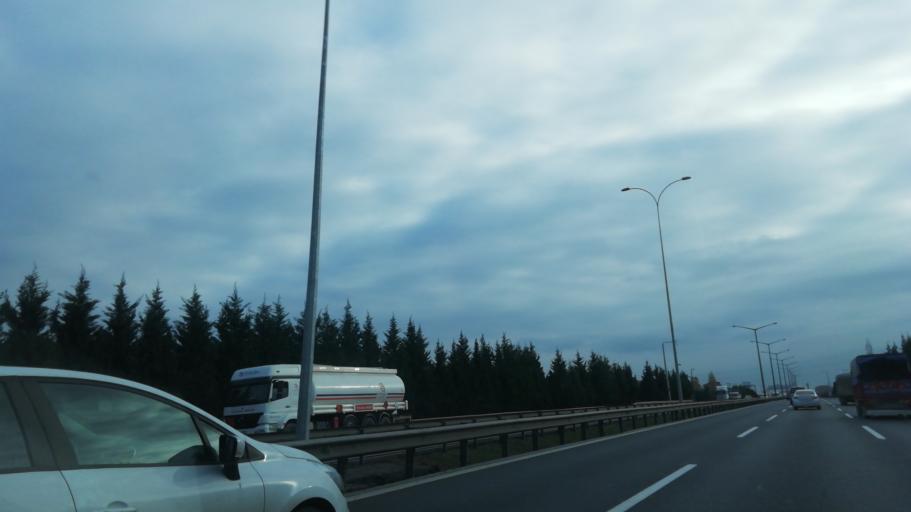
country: TR
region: Kocaeli
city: Korfez
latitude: 40.7727
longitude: 29.7686
